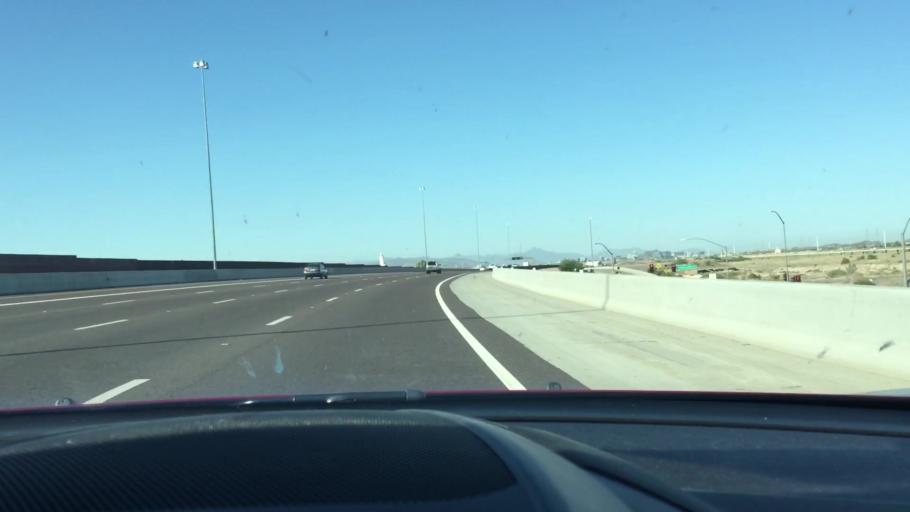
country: US
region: Arizona
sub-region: Maricopa County
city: Mesa
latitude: 33.4556
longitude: -111.8370
